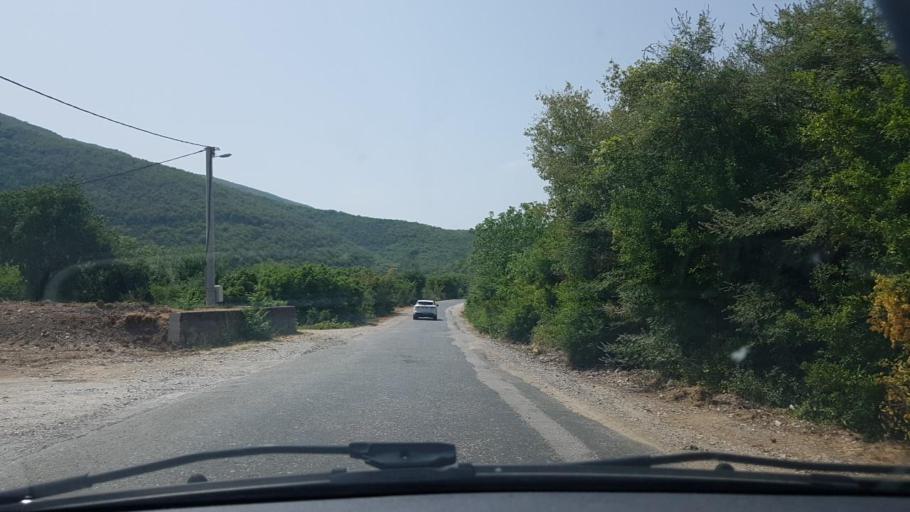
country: BA
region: Federation of Bosnia and Herzegovina
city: Tasovcici
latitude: 43.0222
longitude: 17.7616
